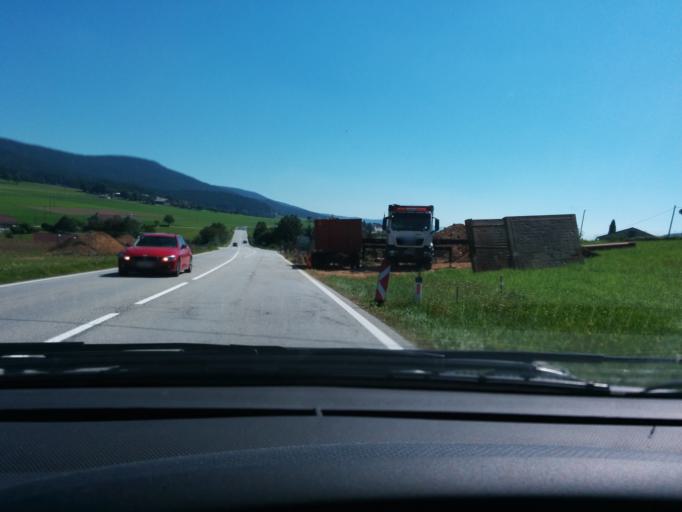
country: AT
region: Upper Austria
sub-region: Politischer Bezirk Rohrbach
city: Ulrichsberg
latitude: 48.6750
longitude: 13.9168
